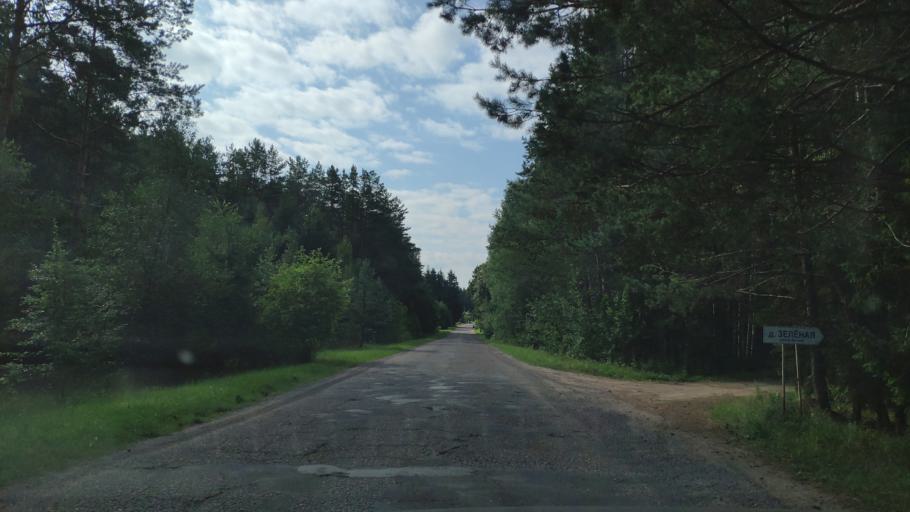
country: BY
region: Minsk
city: Zaslawye
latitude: 53.9805
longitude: 27.2894
